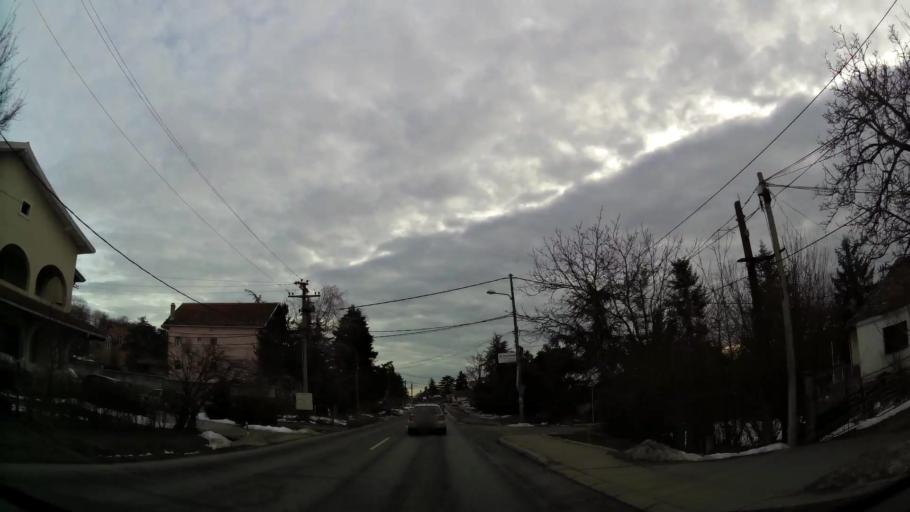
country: RS
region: Central Serbia
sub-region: Belgrade
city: Rakovica
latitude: 44.7336
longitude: 20.4832
